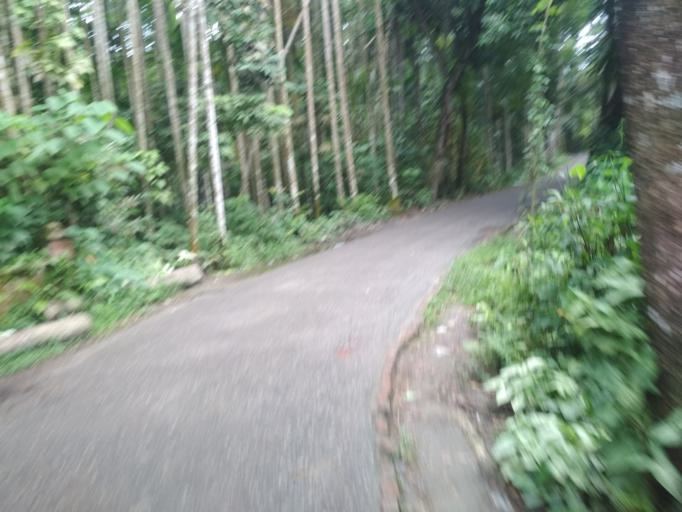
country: BD
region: Chittagong
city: Lakshmipur
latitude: 22.9662
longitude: 90.8007
